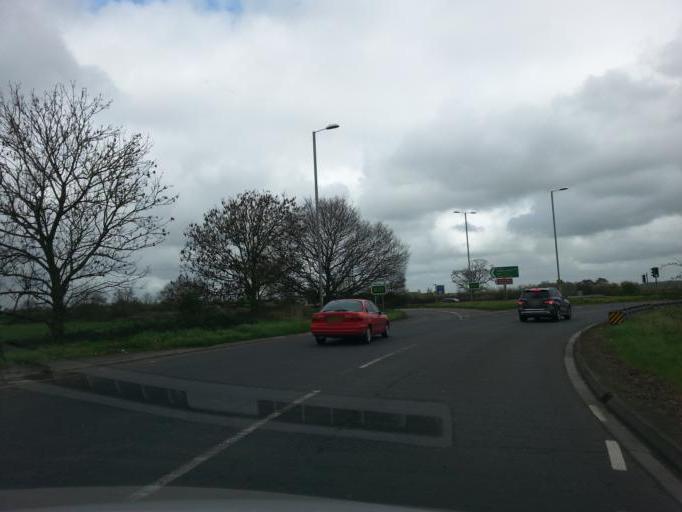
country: GB
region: England
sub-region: Somerset
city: Ilchester
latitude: 51.0240
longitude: -2.6639
